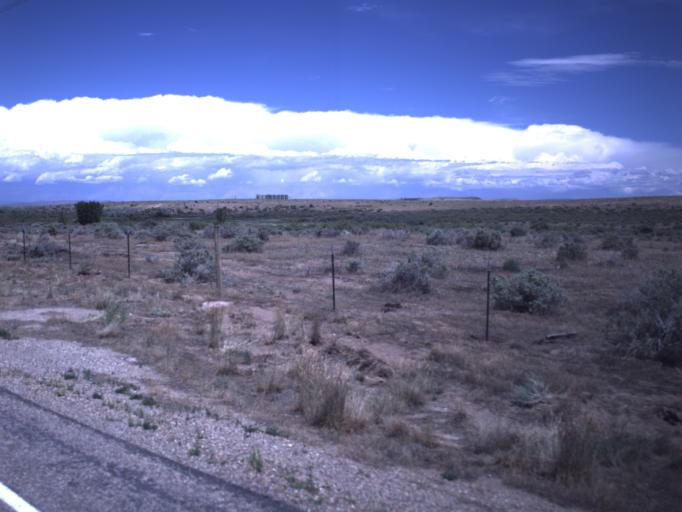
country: US
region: Utah
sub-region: Uintah County
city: Naples
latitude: 40.1325
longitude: -109.6638
